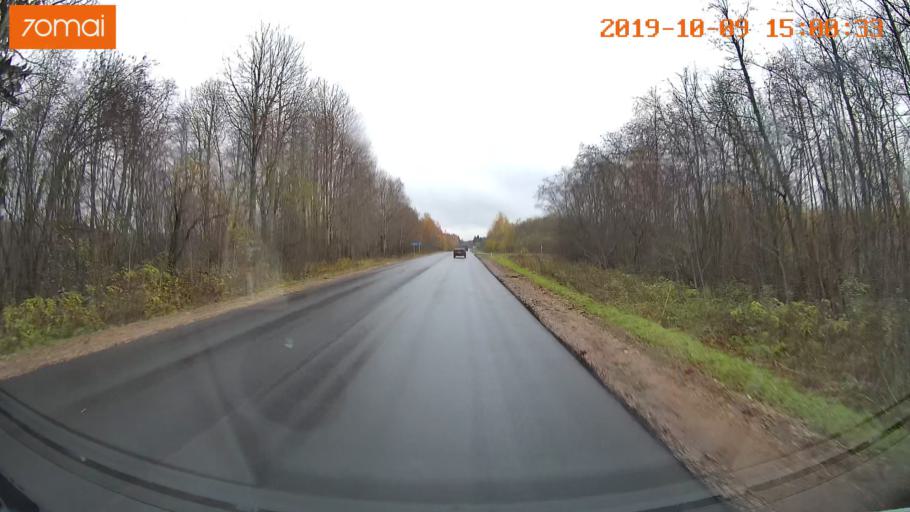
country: RU
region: Kostroma
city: Chistyye Bory
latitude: 58.3081
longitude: 41.6783
